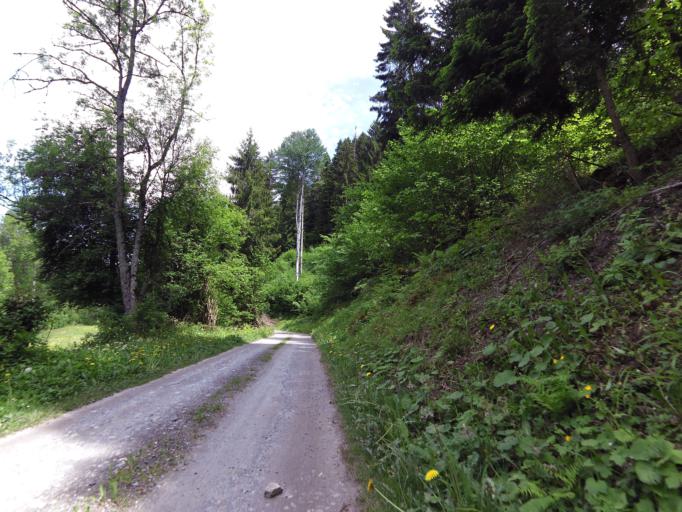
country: CH
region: Grisons
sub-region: Surselva District
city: Breil
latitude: 46.7591
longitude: 9.0981
